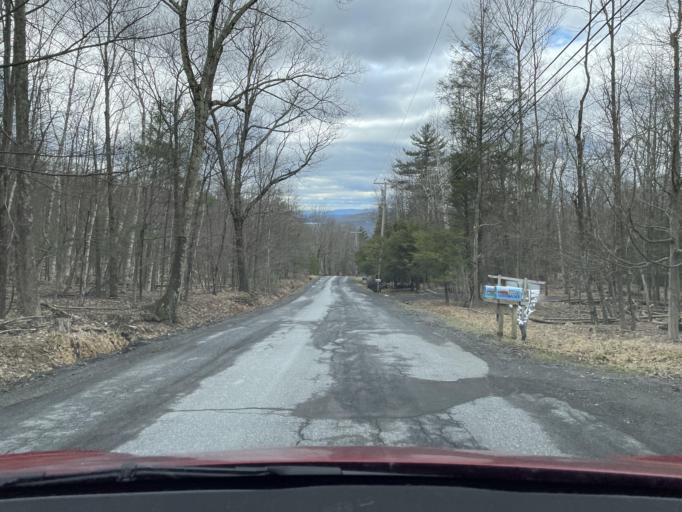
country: US
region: New York
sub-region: Ulster County
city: Woodstock
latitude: 42.0679
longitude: -74.1222
